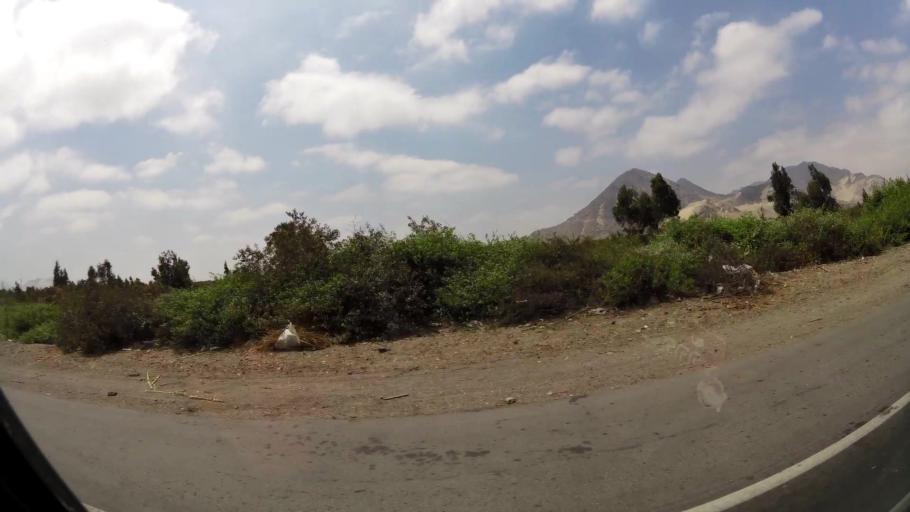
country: PE
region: La Libertad
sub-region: Ascope
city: Paijan
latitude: -7.6752
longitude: -79.3257
